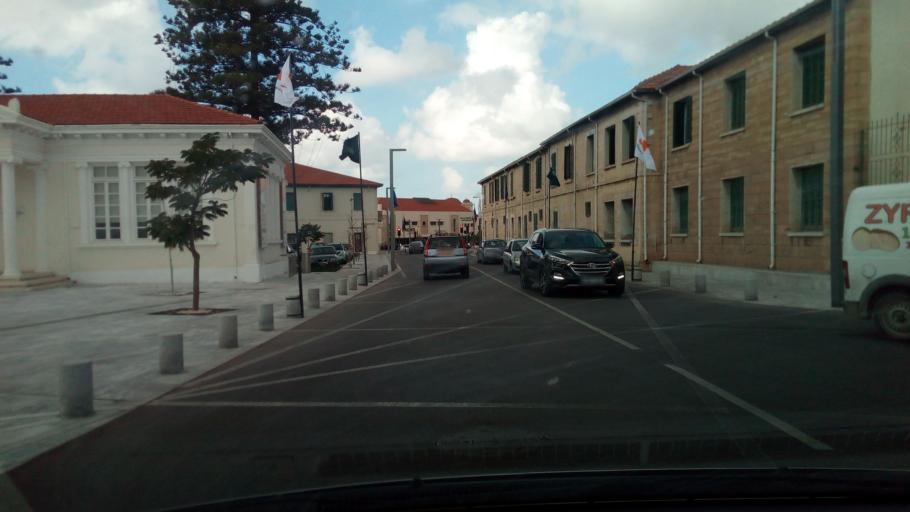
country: CY
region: Pafos
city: Paphos
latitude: 34.7747
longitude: 32.4227
